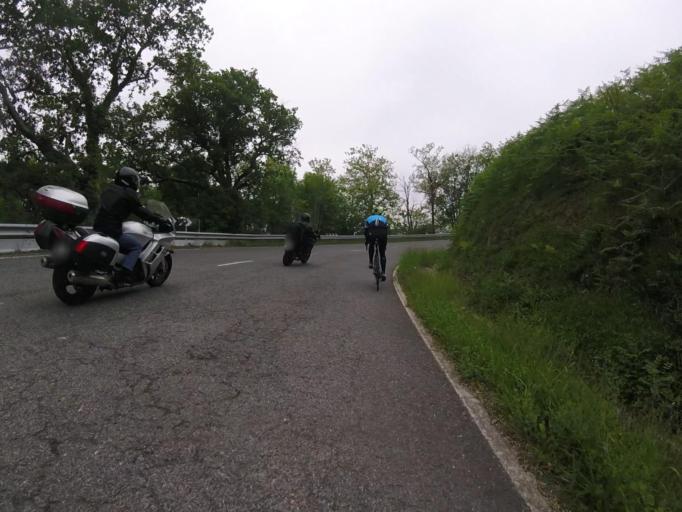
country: ES
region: Navarre
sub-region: Provincia de Navarra
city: Zugarramurdi
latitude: 43.2682
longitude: -1.4959
